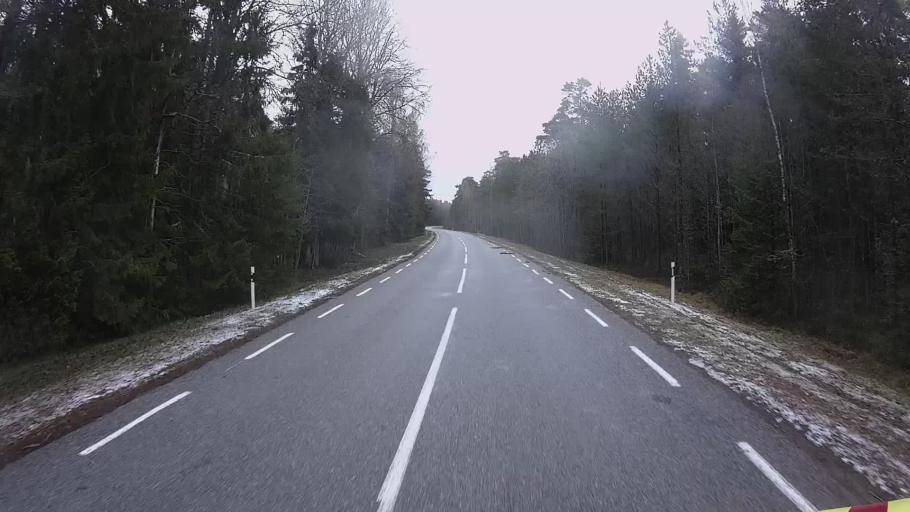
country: EE
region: Hiiumaa
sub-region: Kaerdla linn
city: Kardla
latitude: 59.0499
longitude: 22.6819
